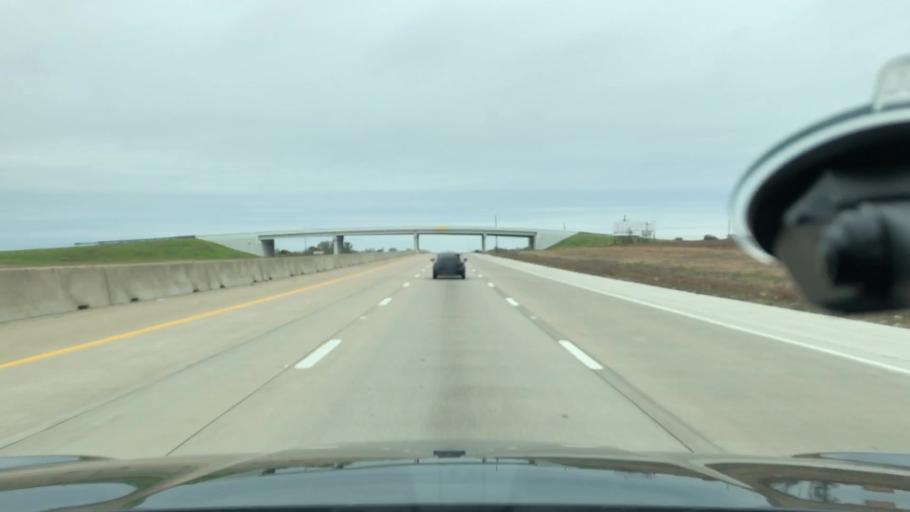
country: US
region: Texas
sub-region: Ellis County
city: Nash
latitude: 32.2973
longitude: -96.8652
